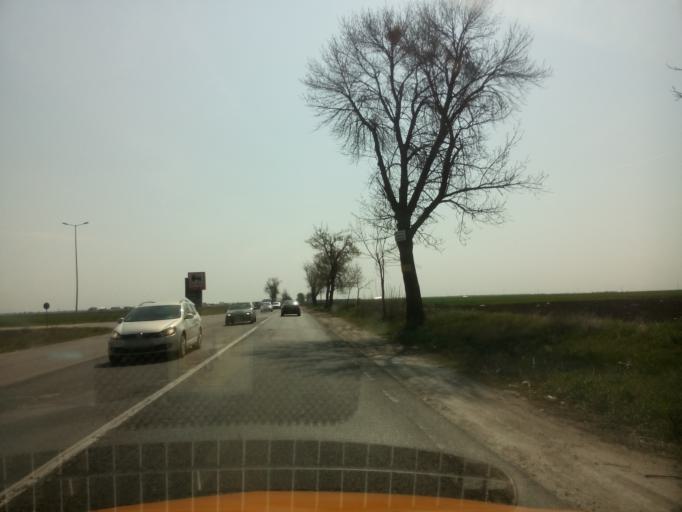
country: RO
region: Ilfov
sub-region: Comuna Glina
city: Glina
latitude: 44.3492
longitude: 26.2191
